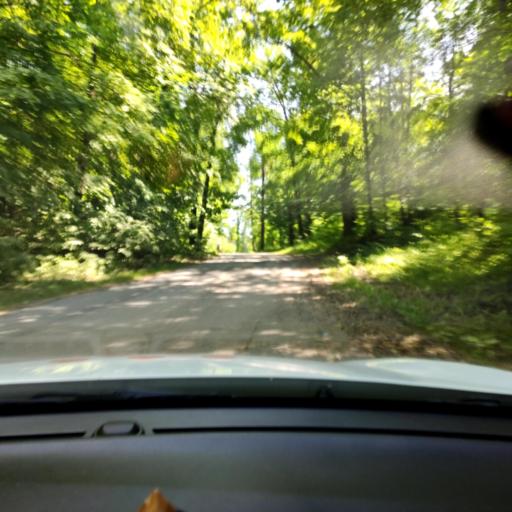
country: RU
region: Tatarstan
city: Sviyazhsk
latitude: 55.7788
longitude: 48.7938
